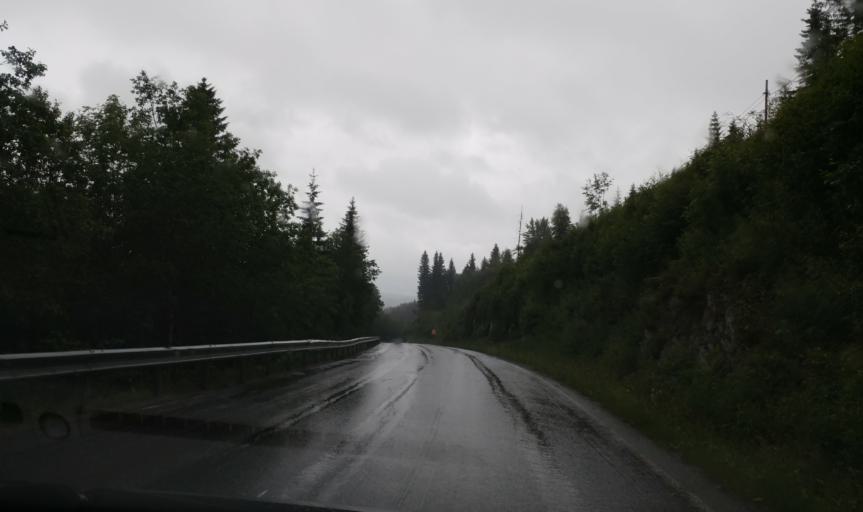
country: NO
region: Sor-Trondelag
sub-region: Selbu
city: Mebonden
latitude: 63.3092
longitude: 11.0795
